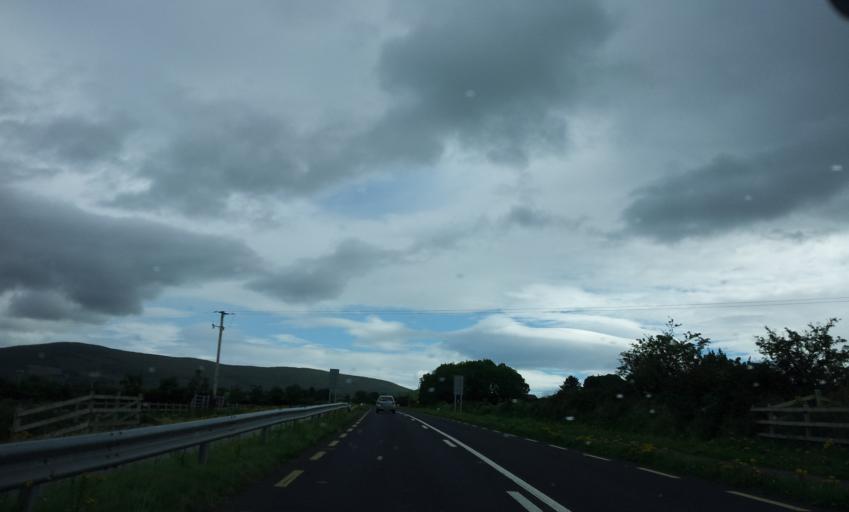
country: IE
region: Munster
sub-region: Ciarrai
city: Dingle
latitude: 52.1555
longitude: -10.0439
